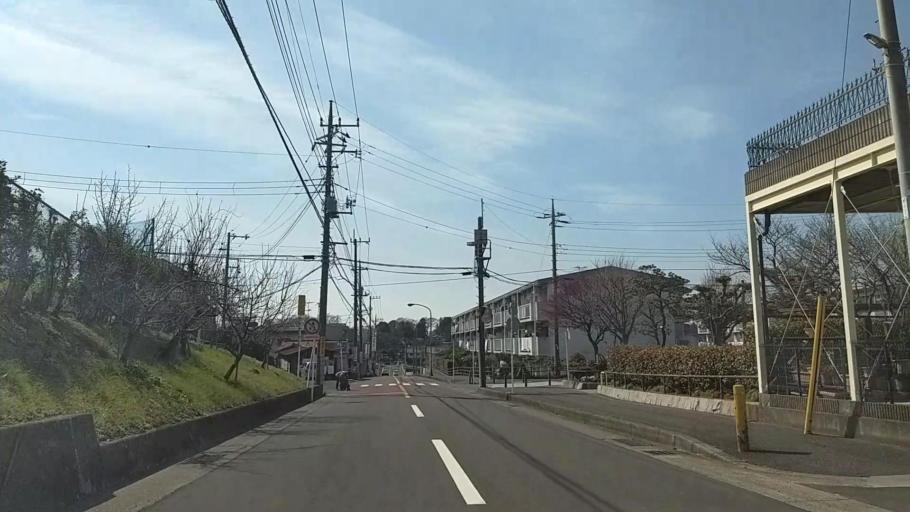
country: JP
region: Kanagawa
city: Fujisawa
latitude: 35.4105
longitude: 139.4584
